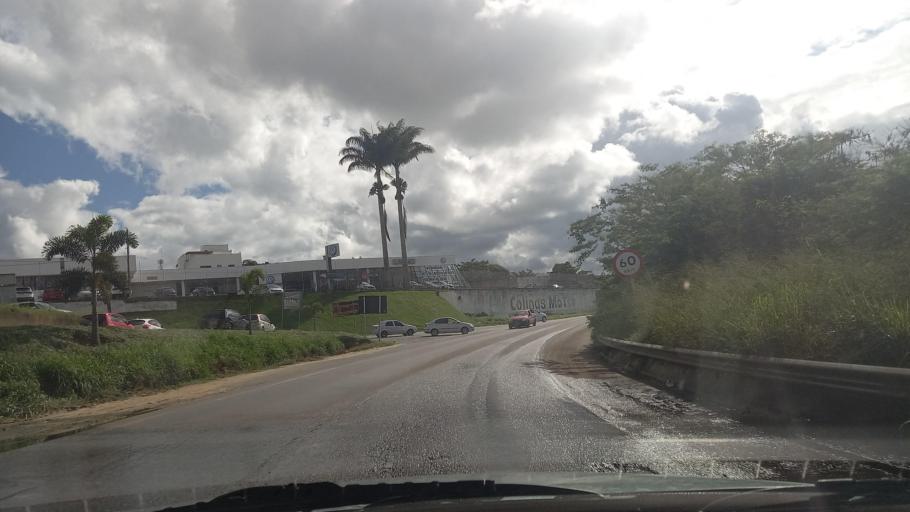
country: BR
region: Pernambuco
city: Garanhuns
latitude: -8.8794
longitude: -36.4792
